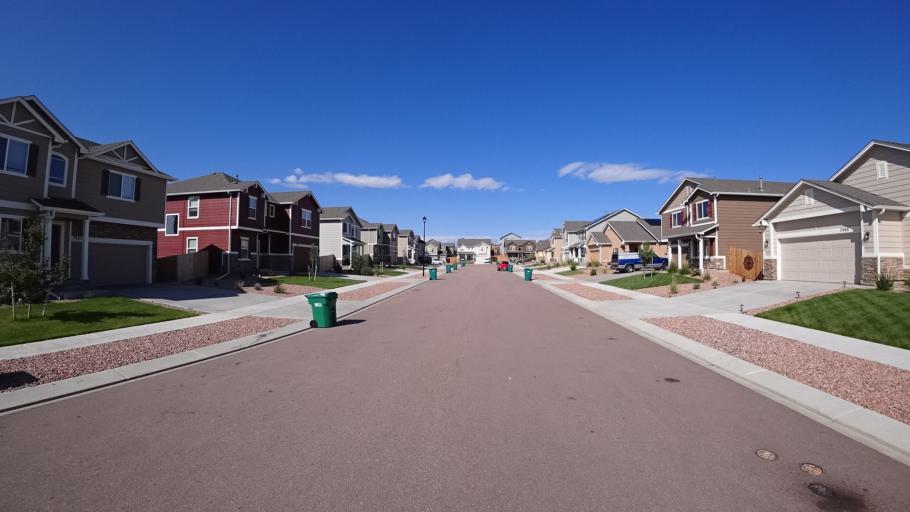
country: US
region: Colorado
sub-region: El Paso County
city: Cimarron Hills
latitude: 38.9337
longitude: -104.6940
